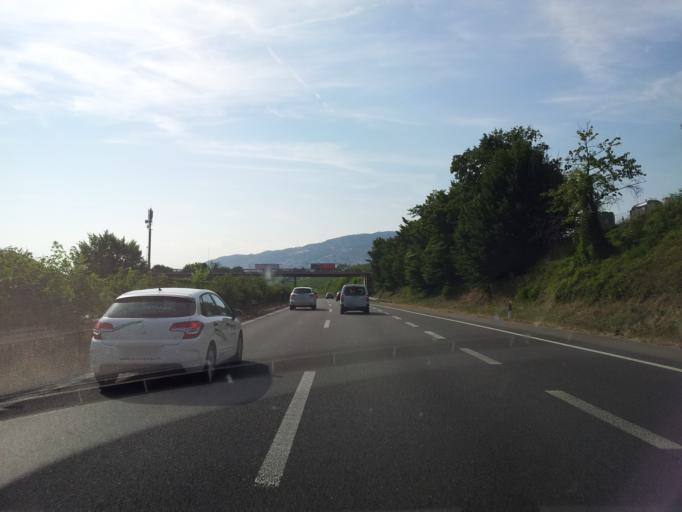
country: CH
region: Vaud
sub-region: Riviera-Pays-d'Enhaut District
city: Le Chatelard
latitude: 46.4546
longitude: 6.8944
